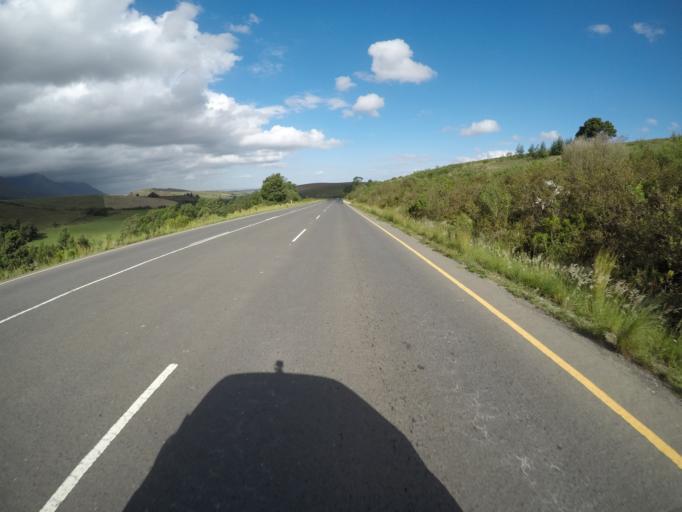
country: ZA
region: Western Cape
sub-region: Overberg District Municipality
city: Swellendam
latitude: -33.9954
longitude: 20.3540
